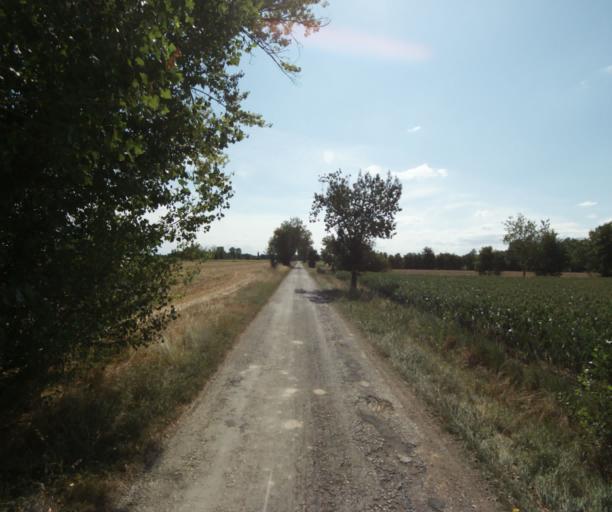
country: FR
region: Midi-Pyrenees
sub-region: Departement de la Haute-Garonne
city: Revel
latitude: 43.4950
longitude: 1.9661
